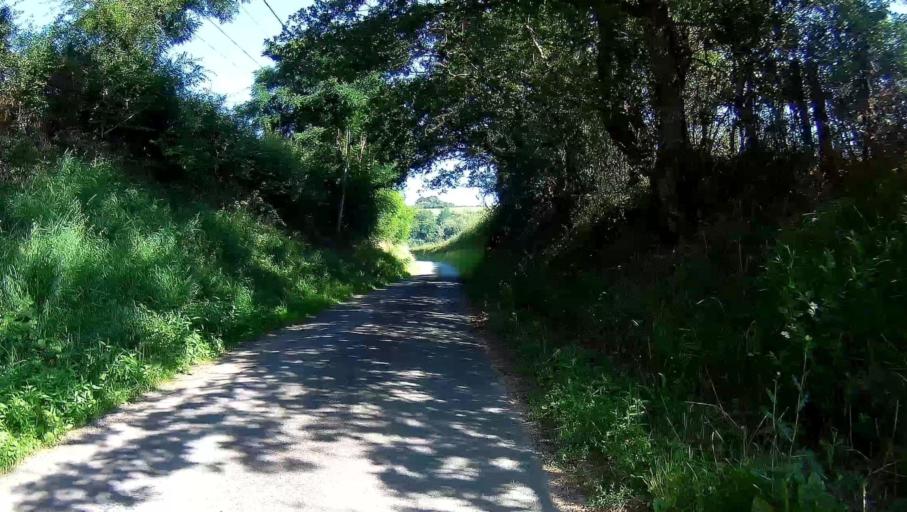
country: FR
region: Bourgogne
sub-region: Departement de Saone-et-Loire
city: Couches
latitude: 46.8439
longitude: 4.5738
